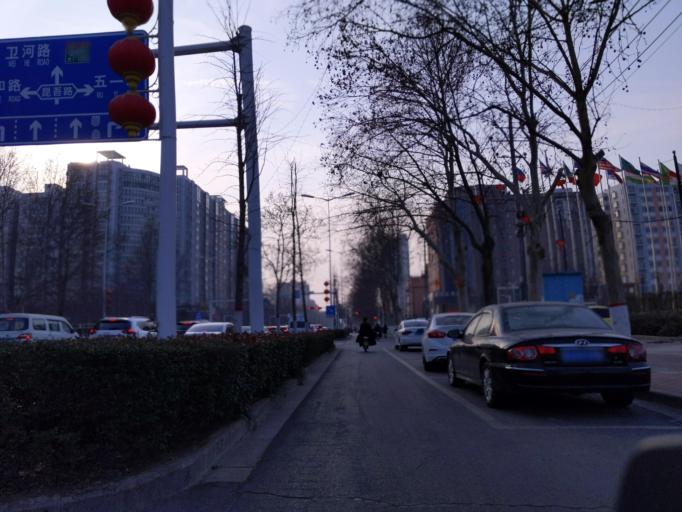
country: CN
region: Henan Sheng
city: Puyang
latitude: 35.7814
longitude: 115.0162
